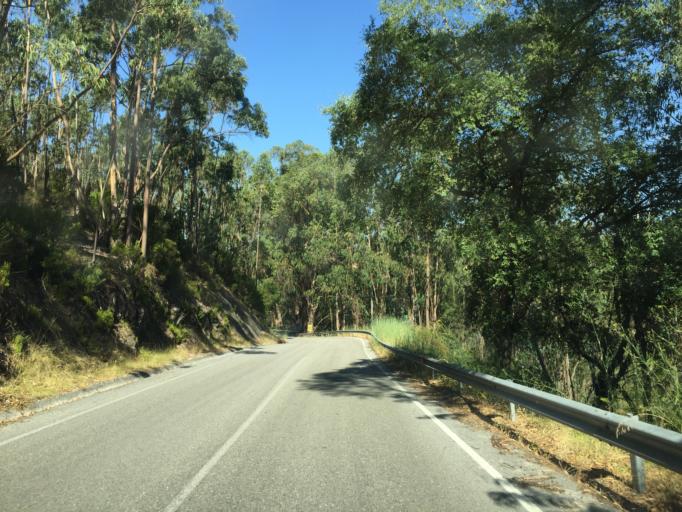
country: PT
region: Santarem
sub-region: Tomar
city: Tomar
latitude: 39.6051
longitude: -8.3442
